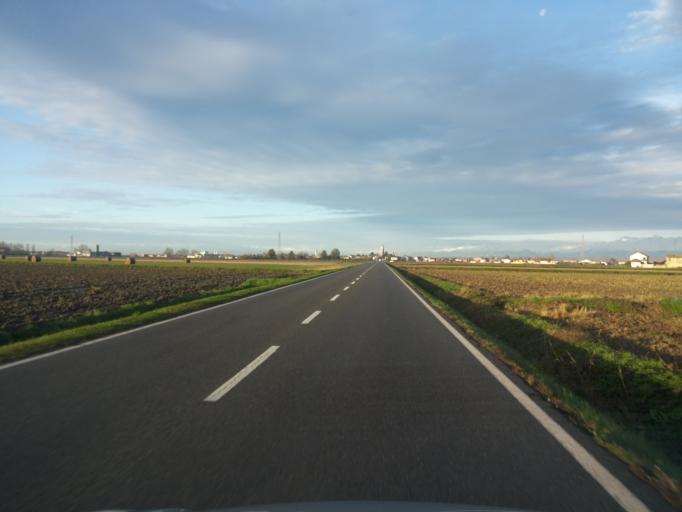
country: IT
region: Piedmont
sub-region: Provincia di Vercelli
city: Crova
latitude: 45.3441
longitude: 8.1964
